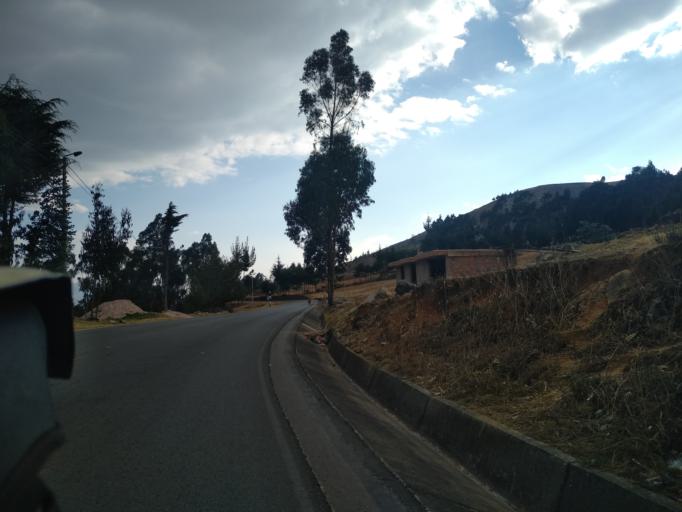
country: PE
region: Cajamarca
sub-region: Provincia de Cajamarca
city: Llacanora
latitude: -7.1463
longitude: -78.4095
